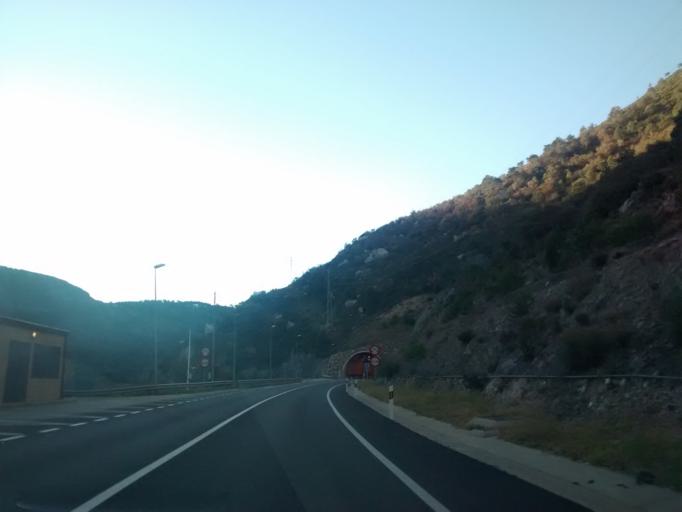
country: ES
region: Catalonia
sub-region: Provincia de Lleida
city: Coll de Nargo
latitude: 42.1342
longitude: 1.3098
